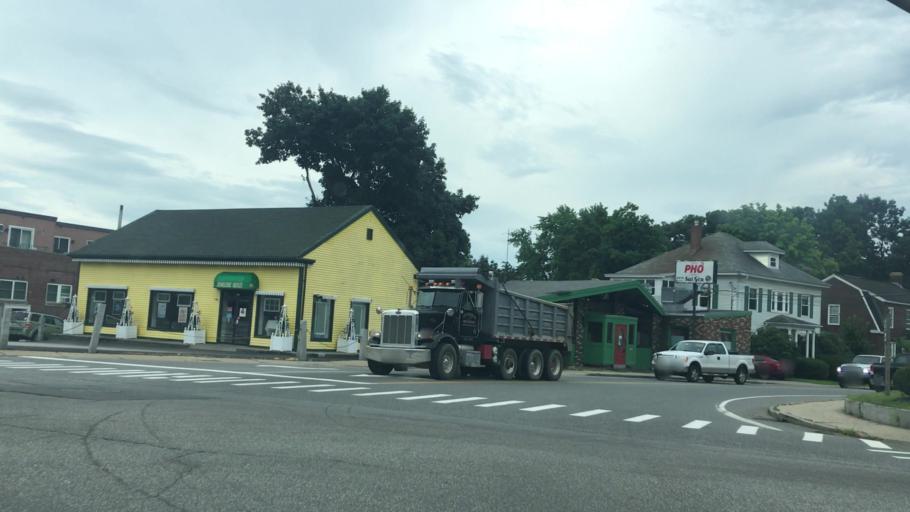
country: US
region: Maine
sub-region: York County
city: Sanford (historical)
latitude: 43.4408
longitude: -70.7776
